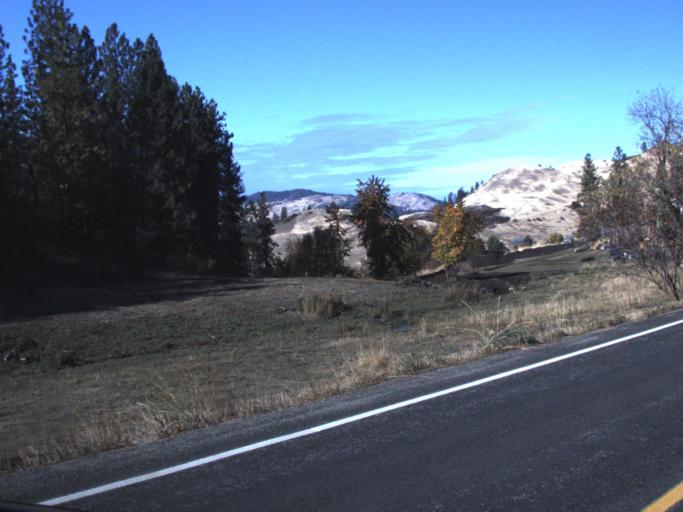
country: US
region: Washington
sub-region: Lincoln County
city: Davenport
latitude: 48.1116
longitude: -118.2028
